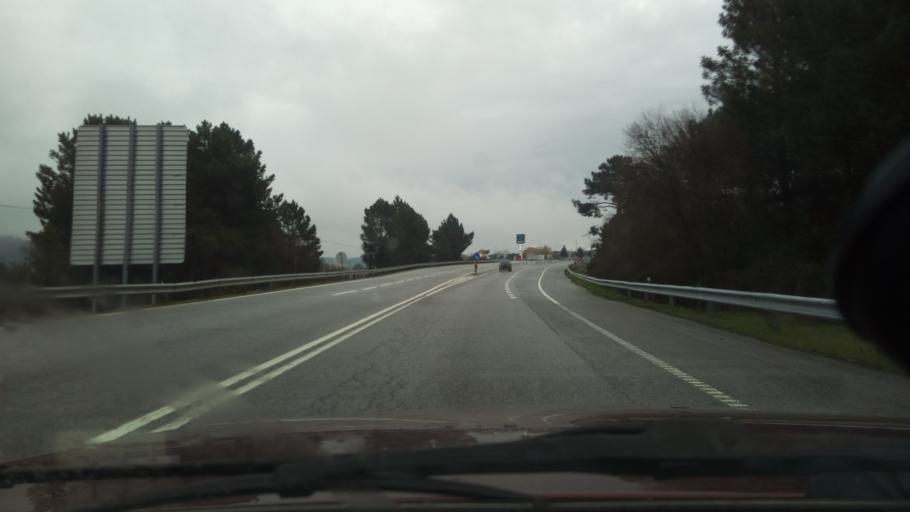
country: PT
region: Guarda
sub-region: Fornos de Algodres
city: Fornos de Algodres
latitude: 40.6171
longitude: -7.6180
